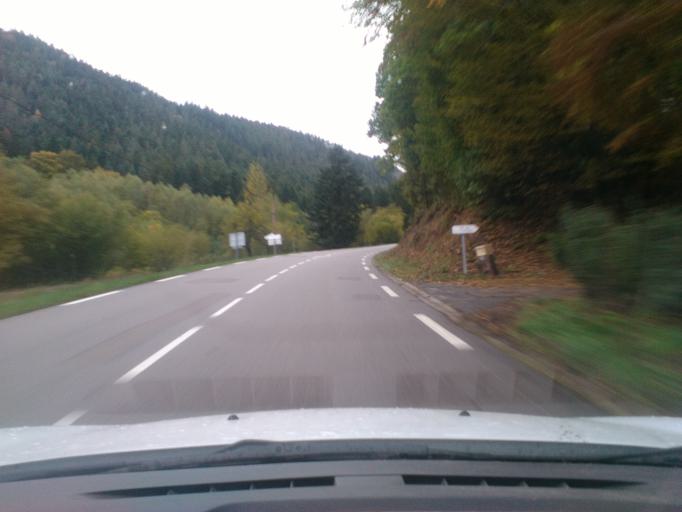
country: FR
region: Lorraine
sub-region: Departement des Vosges
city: Taintrux
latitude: 48.2748
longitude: 6.8940
